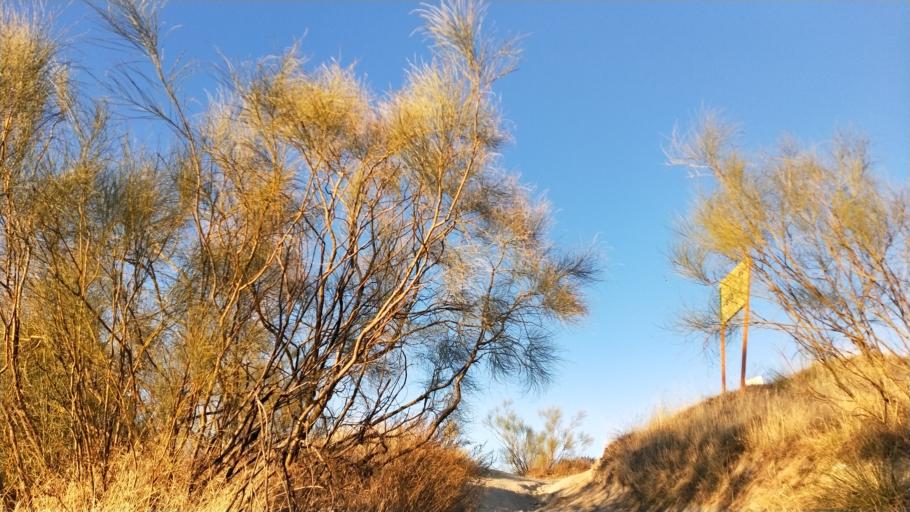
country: ES
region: Andalusia
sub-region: Provincia de Granada
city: Beas de Granada
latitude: 37.2060
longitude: -3.4976
